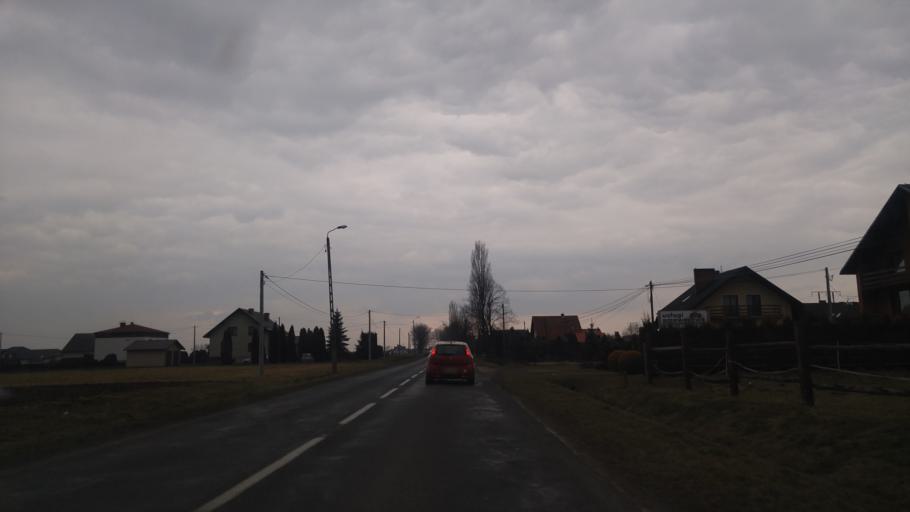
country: PL
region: Silesian Voivodeship
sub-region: Powiat cieszynski
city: Chybie
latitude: 49.9476
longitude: 18.8418
